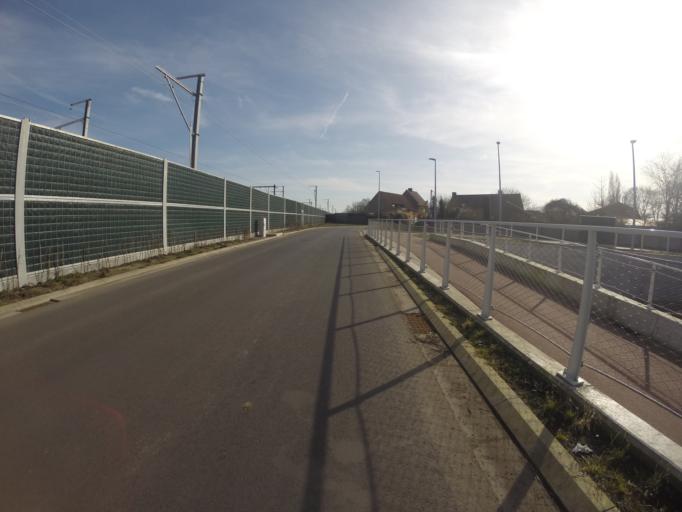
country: BE
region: Flanders
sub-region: Provincie West-Vlaanderen
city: Oostkamp
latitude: 51.1521
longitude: 3.2624
